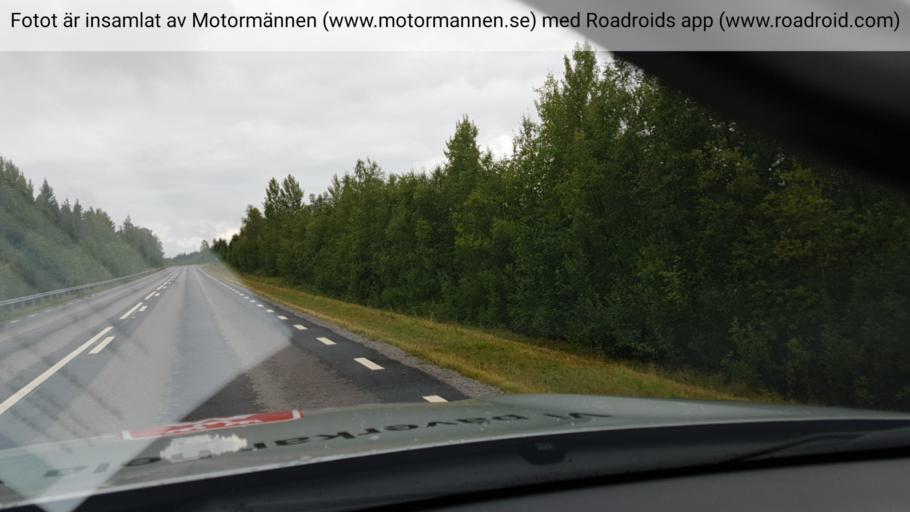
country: SE
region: Norrbotten
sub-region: Gallivare Kommun
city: Gaellivare
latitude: 66.3794
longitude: 20.7100
